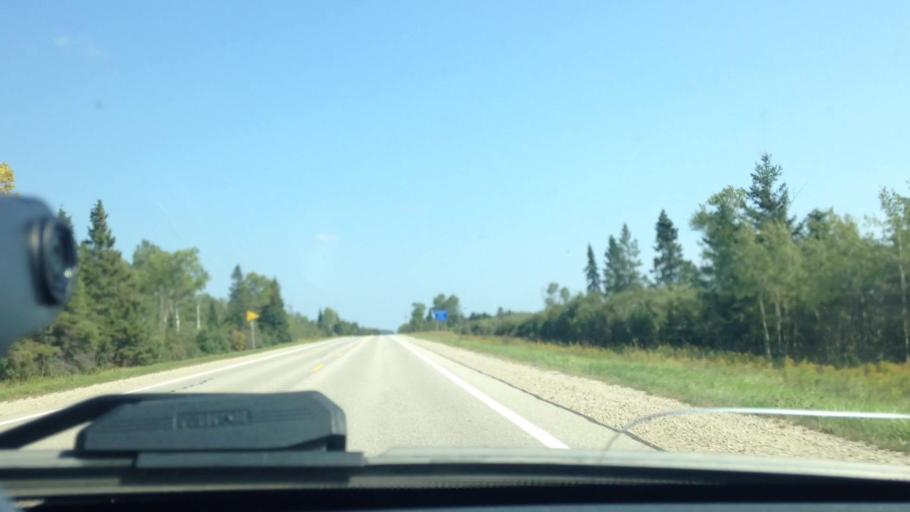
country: US
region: Michigan
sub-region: Luce County
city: Newberry
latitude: 46.3104
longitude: -85.6028
